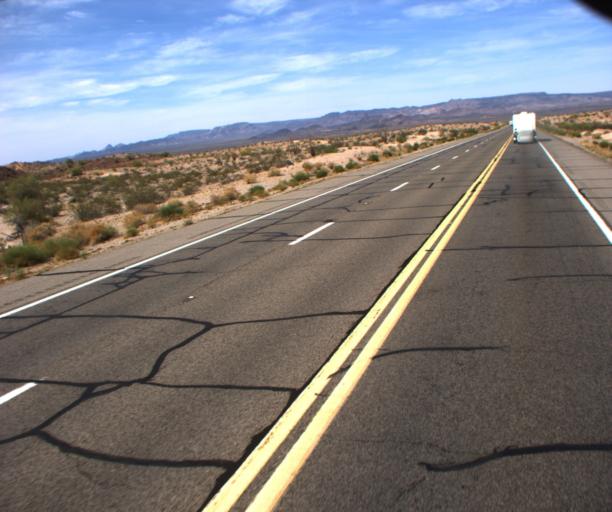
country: US
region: Arizona
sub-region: Mohave County
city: Desert Hills
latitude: 34.6783
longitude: -114.3070
